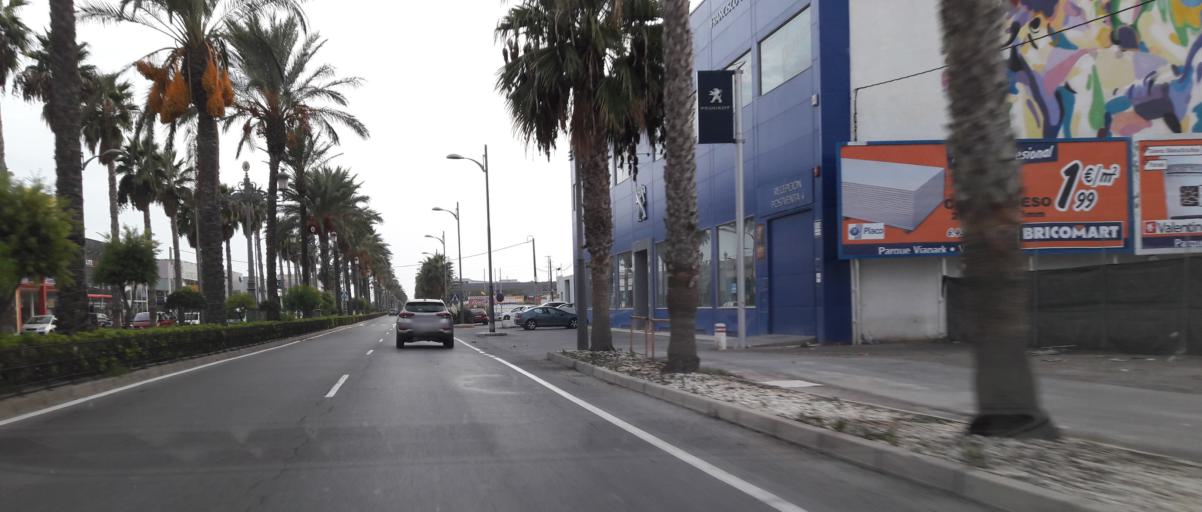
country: ES
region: Andalusia
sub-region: Provincia de Almeria
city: Roquetas de Mar
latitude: 36.7853
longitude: -2.6072
